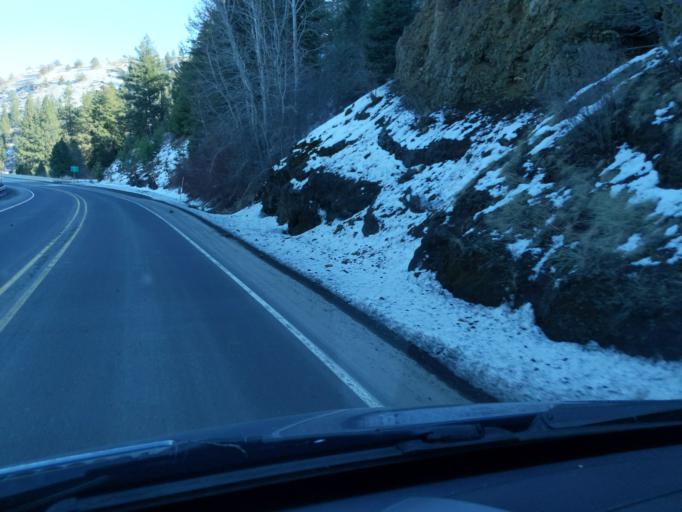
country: US
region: Oregon
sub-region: Grant County
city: John Day
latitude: 44.8357
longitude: -119.0346
